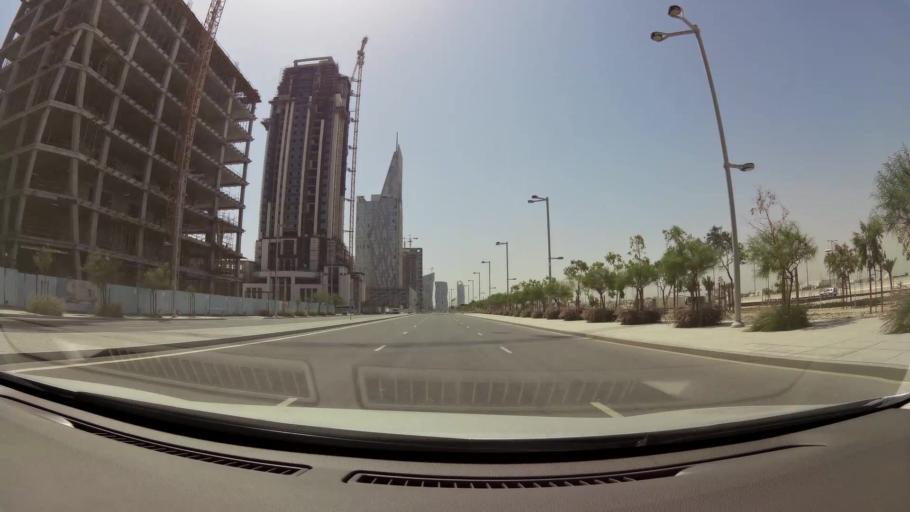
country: QA
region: Baladiyat Umm Salal
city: Umm Salal Muhammad
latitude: 25.3957
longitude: 51.5177
